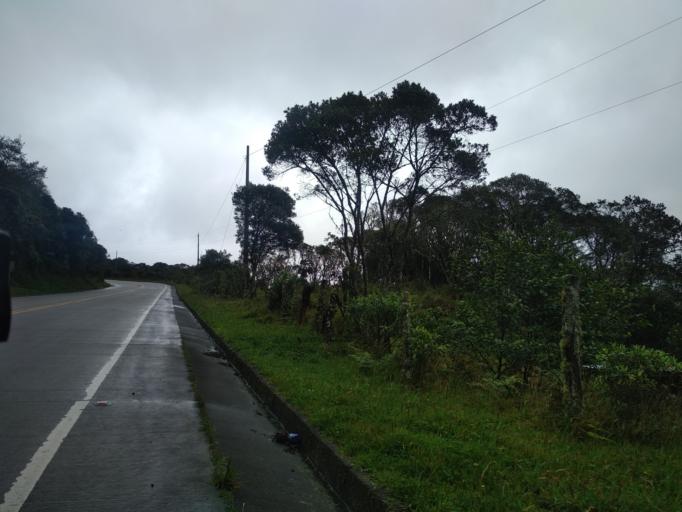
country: EC
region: Loja
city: Catamayo
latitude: -3.8618
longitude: -79.2822
